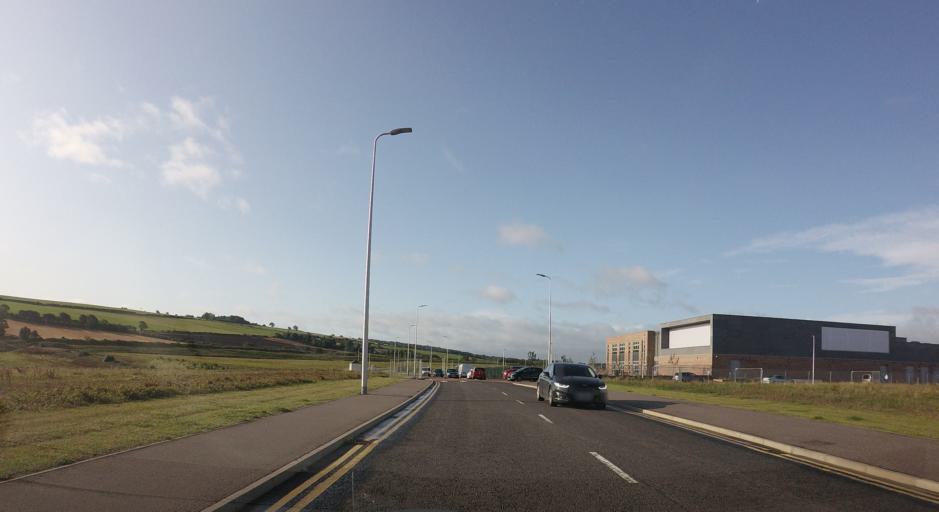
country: GB
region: Scotland
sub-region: East Lothian
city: Prestonpans
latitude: 55.9386
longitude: -3.0032
